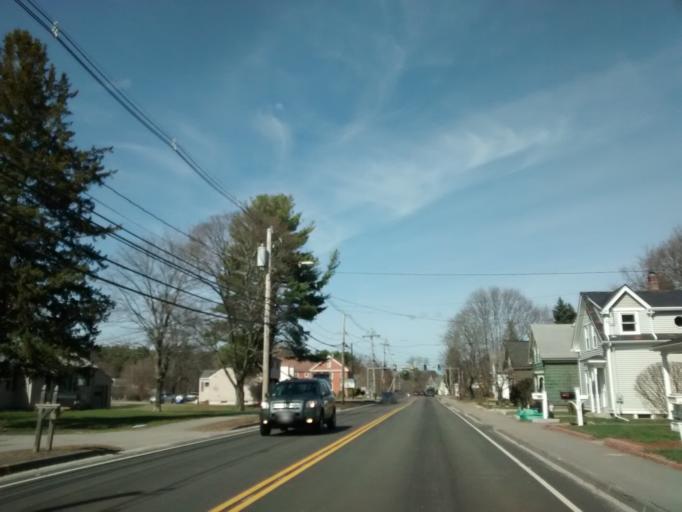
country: US
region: Massachusetts
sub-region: Norfolk County
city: Bellingham
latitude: 42.1204
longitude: -71.4568
